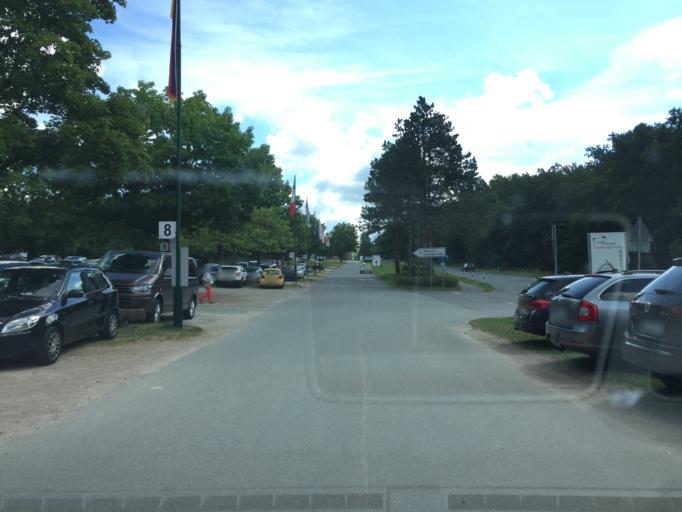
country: DE
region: Lower Saxony
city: Hanstedt
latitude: 53.2359
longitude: 10.0446
